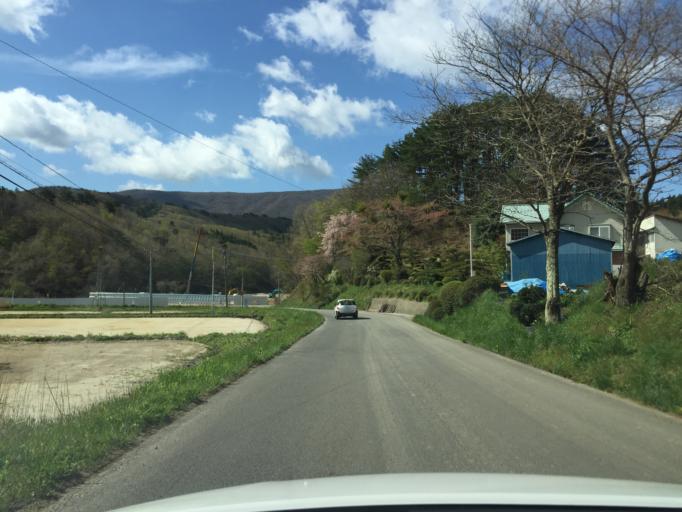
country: JP
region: Fukushima
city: Funehikimachi-funehiki
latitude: 37.5695
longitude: 140.6935
